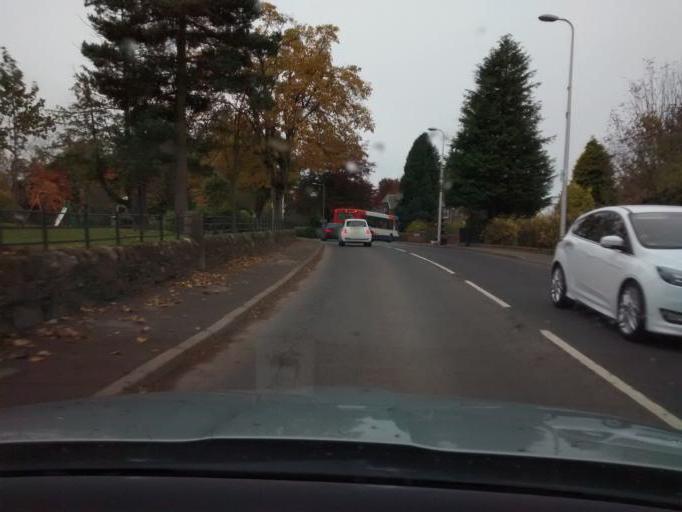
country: GB
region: Scotland
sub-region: Perth and Kinross
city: Auchterarder
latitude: 56.2919
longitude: -3.7179
